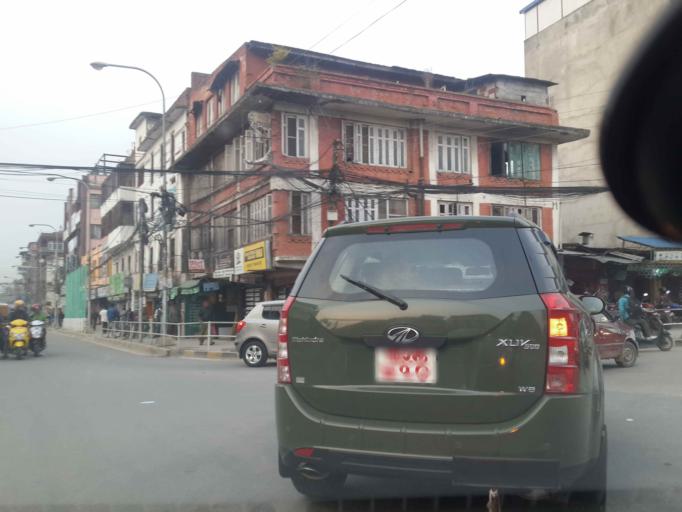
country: NP
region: Central Region
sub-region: Bagmati Zone
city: Kathmandu
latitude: 27.7011
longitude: 85.3222
